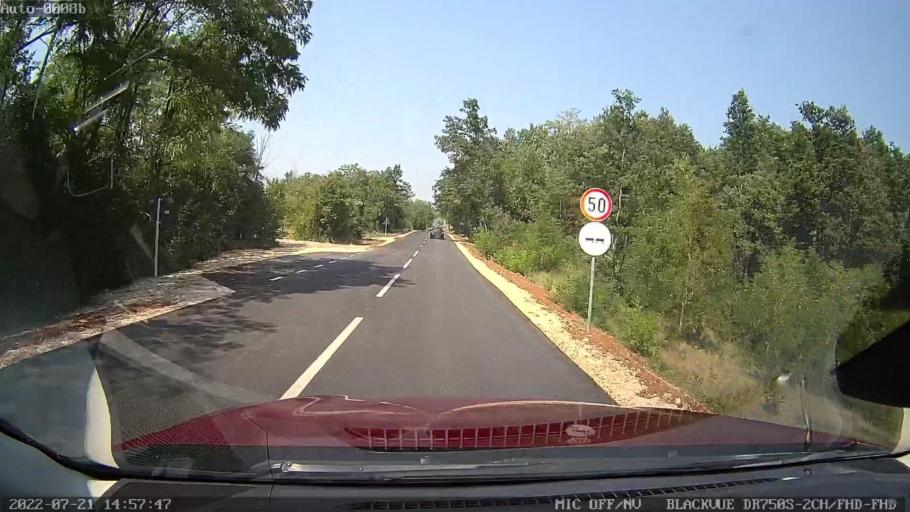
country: HR
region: Istarska
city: Pazin
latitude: 45.2113
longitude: 13.9546
